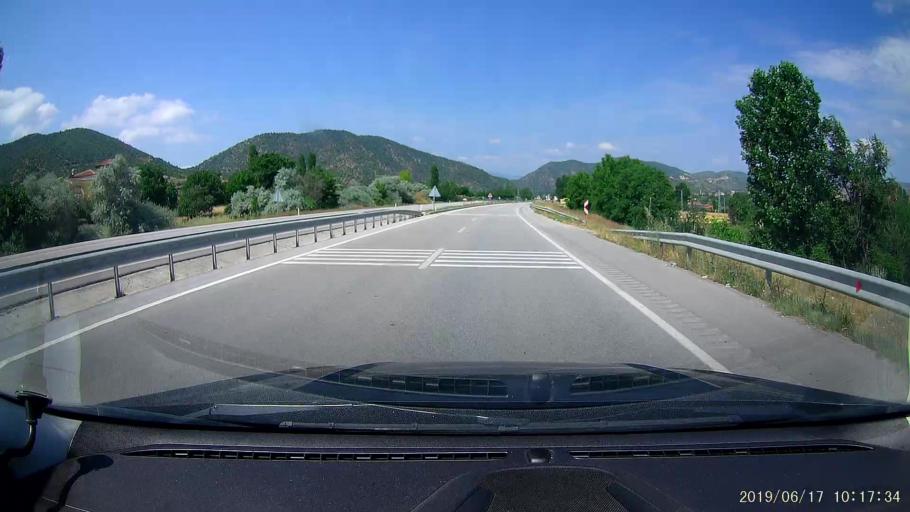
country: TR
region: Corum
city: Osmancik
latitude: 40.9798
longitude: 34.9451
